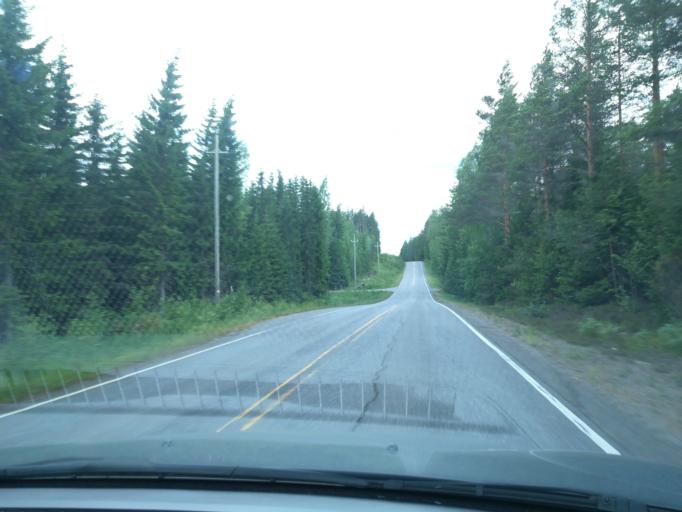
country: FI
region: Southern Savonia
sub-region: Mikkeli
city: Ristiina
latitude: 61.3451
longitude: 27.1759
